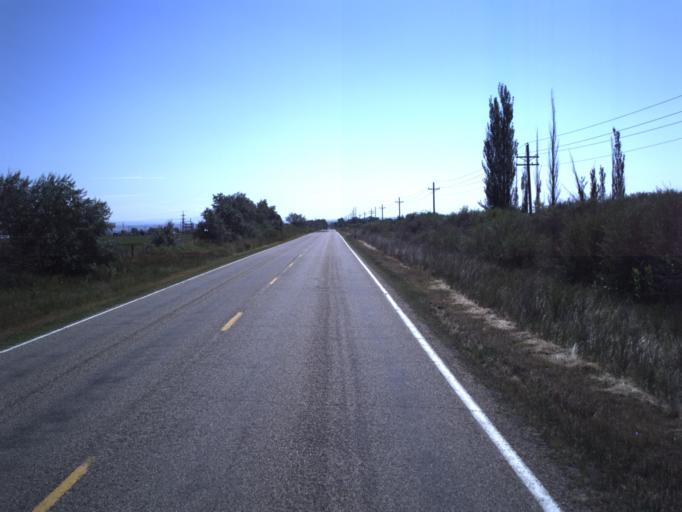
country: US
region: Utah
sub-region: Duchesne County
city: Roosevelt
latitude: 40.2580
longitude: -110.1705
